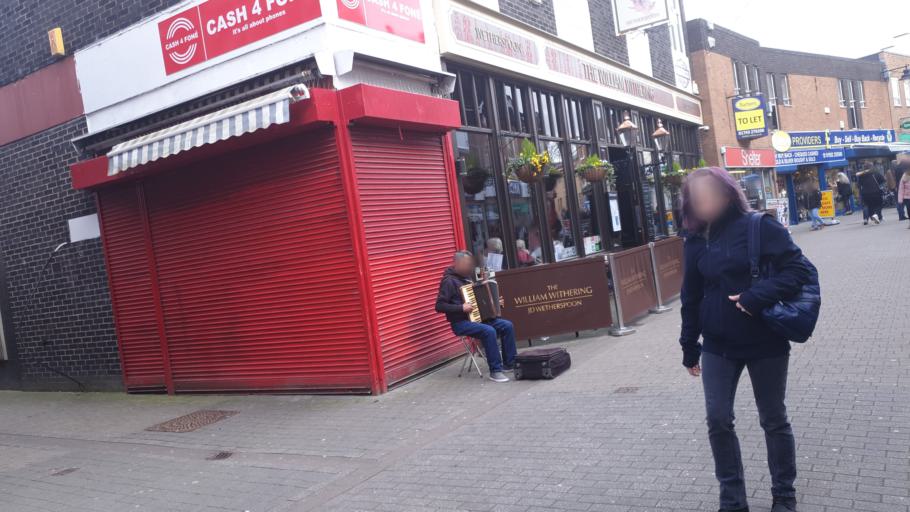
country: GB
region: England
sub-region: Telford and Wrekin
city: Wellington
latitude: 52.7005
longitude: -2.5170
